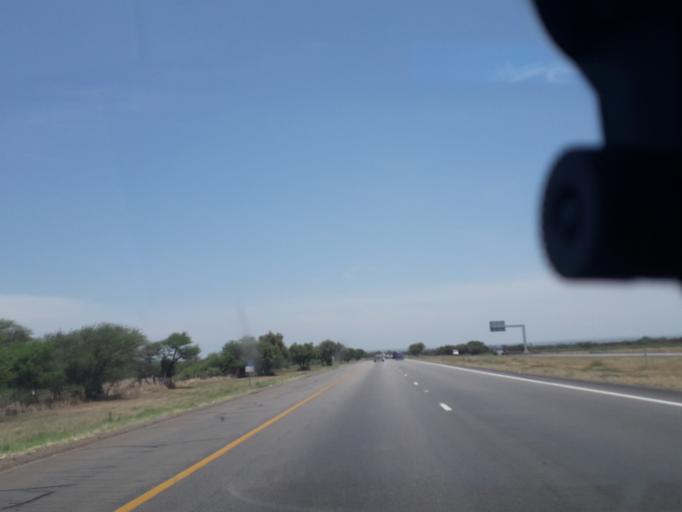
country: ZA
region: North-West
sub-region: Bojanala Platinum District Municipality
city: Makapanstad
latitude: -25.1498
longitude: 28.3087
